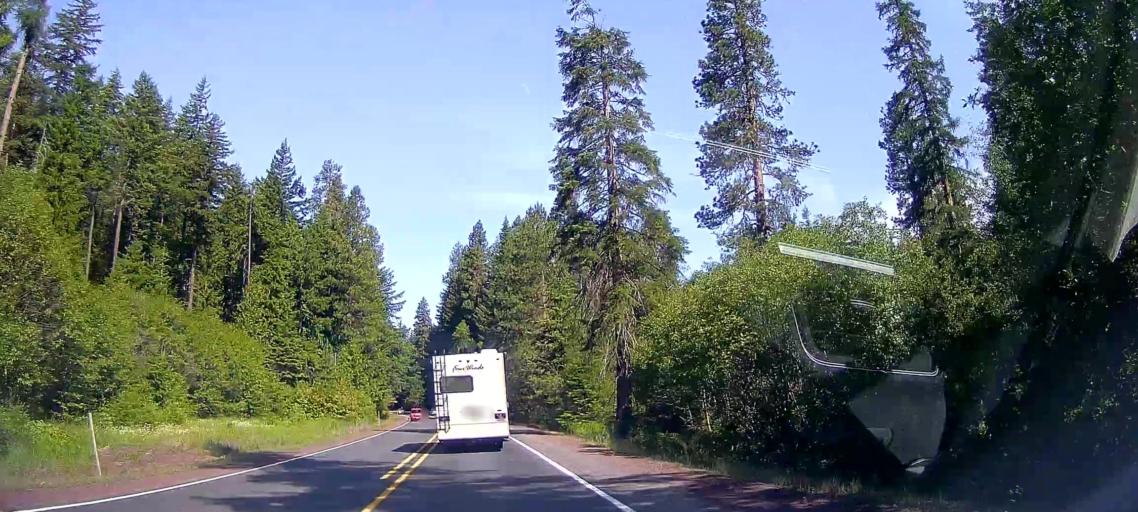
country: US
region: Oregon
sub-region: Jefferson County
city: Warm Springs
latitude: 45.0705
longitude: -121.5279
